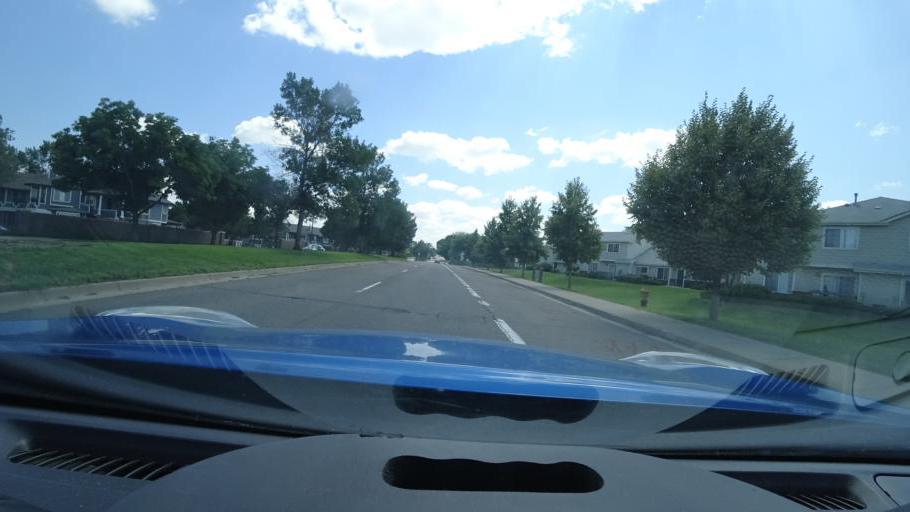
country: US
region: Colorado
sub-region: Arapahoe County
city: Glendale
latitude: 39.6965
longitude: -104.8872
